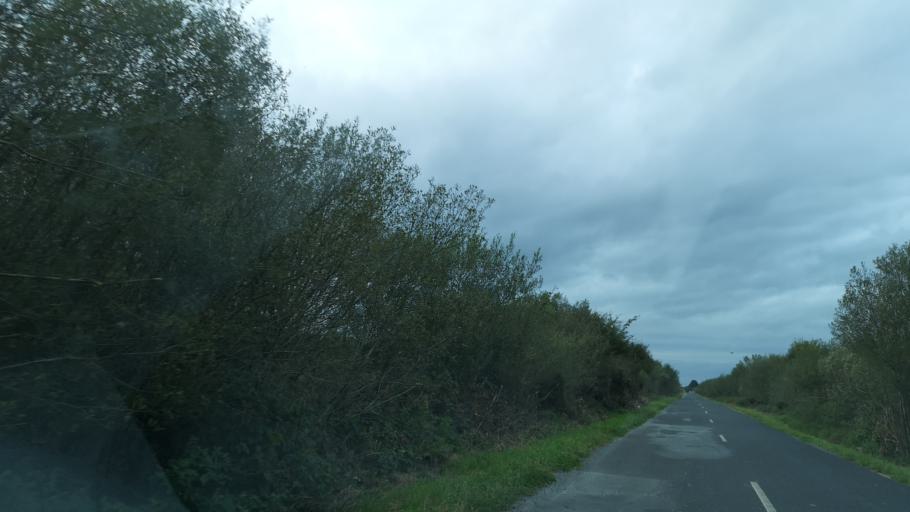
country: IE
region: Leinster
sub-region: Uibh Fhaili
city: Ferbane
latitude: 53.2048
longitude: -7.7845
